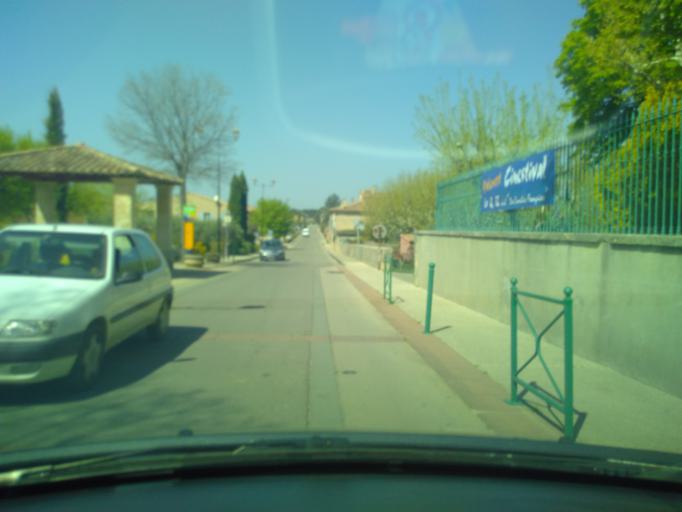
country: FR
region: Provence-Alpes-Cote d'Azur
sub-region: Departement du Vaucluse
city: Malemort-du-Comtat
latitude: 44.0218
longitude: 5.1580
